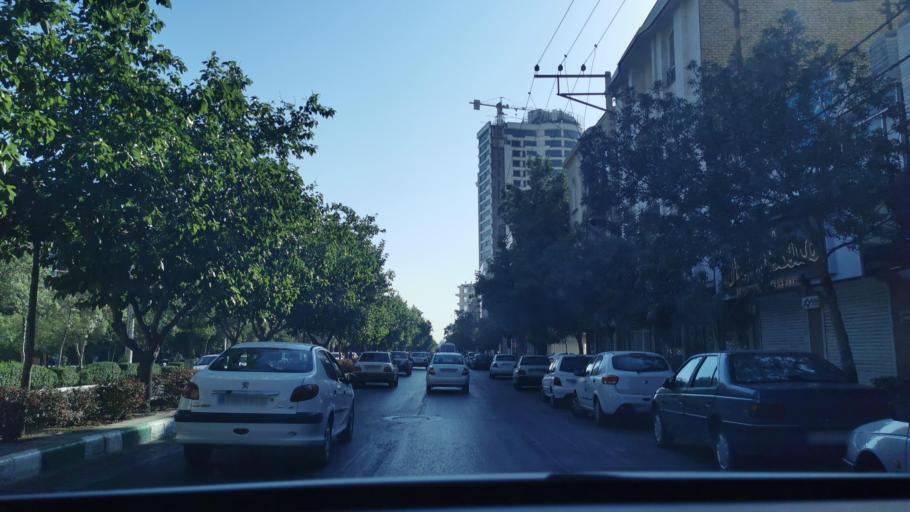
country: IR
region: Razavi Khorasan
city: Mashhad
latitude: 36.3132
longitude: 59.5157
